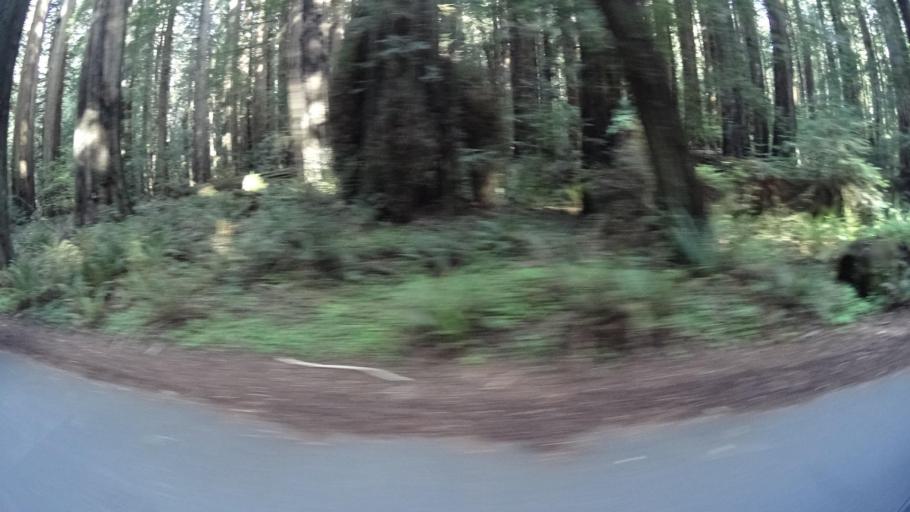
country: US
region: California
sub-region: Humboldt County
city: Rio Dell
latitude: 40.3519
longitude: -123.9949
